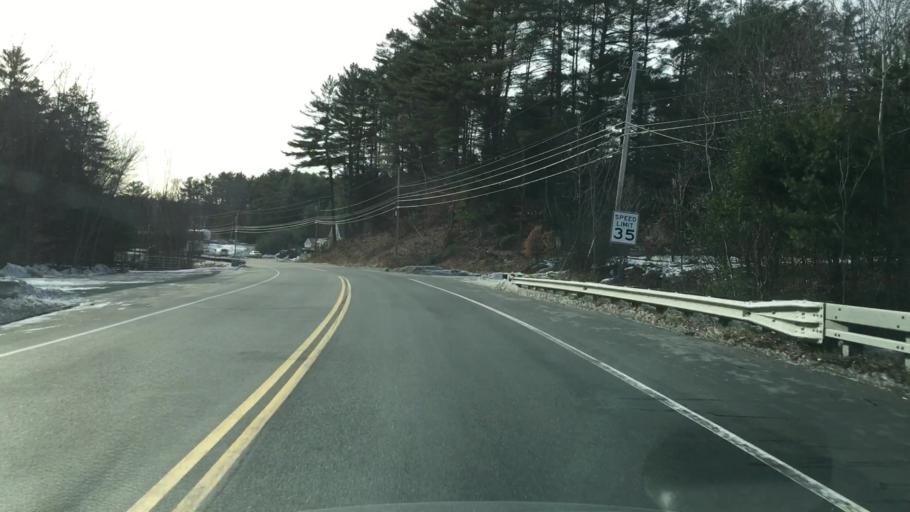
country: US
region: New Hampshire
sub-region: Sullivan County
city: Sunapee
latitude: 43.3781
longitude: -72.1212
